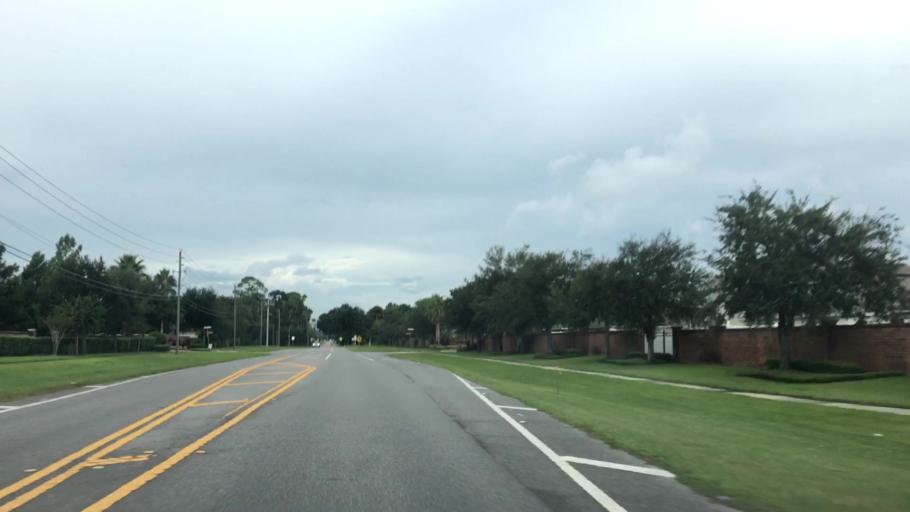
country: US
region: Florida
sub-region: Seminole County
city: Midway
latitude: 28.8013
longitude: -81.2366
